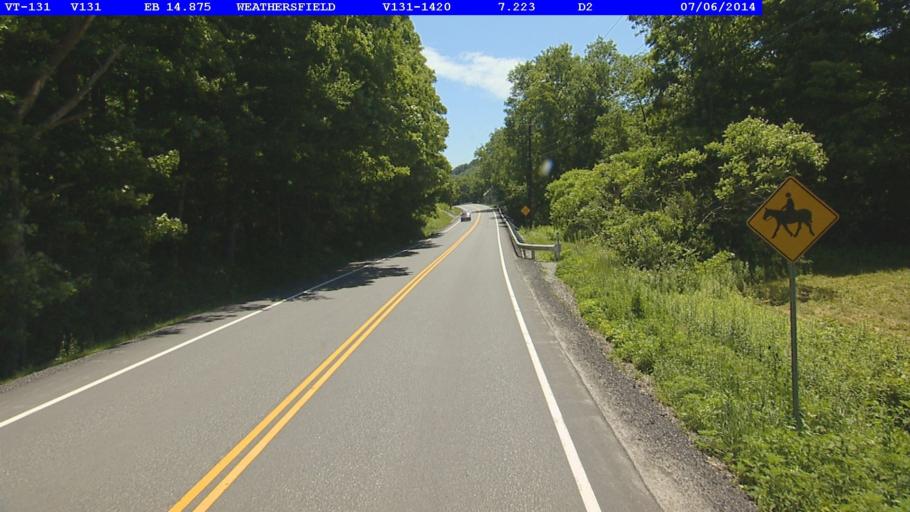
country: US
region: Vermont
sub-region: Windsor County
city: Windsor
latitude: 43.4049
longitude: -72.4319
